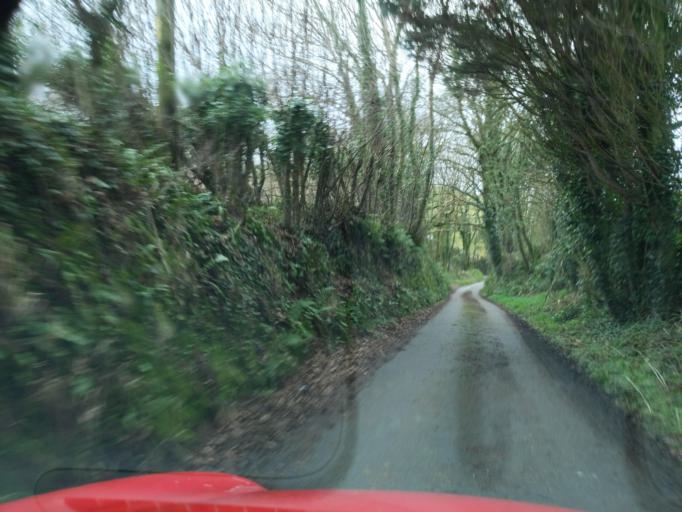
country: GB
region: England
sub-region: Cornwall
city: Duloe
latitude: 50.3512
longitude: -4.5127
